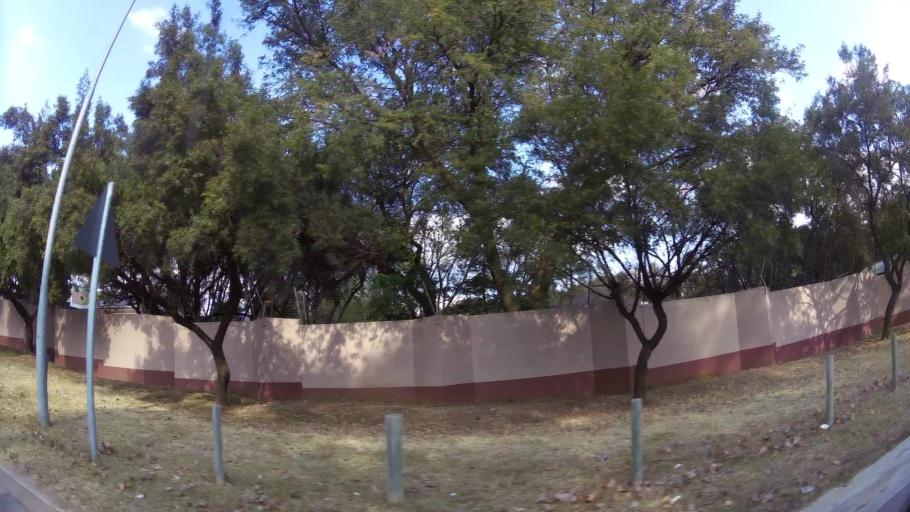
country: ZA
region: Gauteng
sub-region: City of Johannesburg Metropolitan Municipality
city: Diepsloot
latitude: -26.0317
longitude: 28.0164
